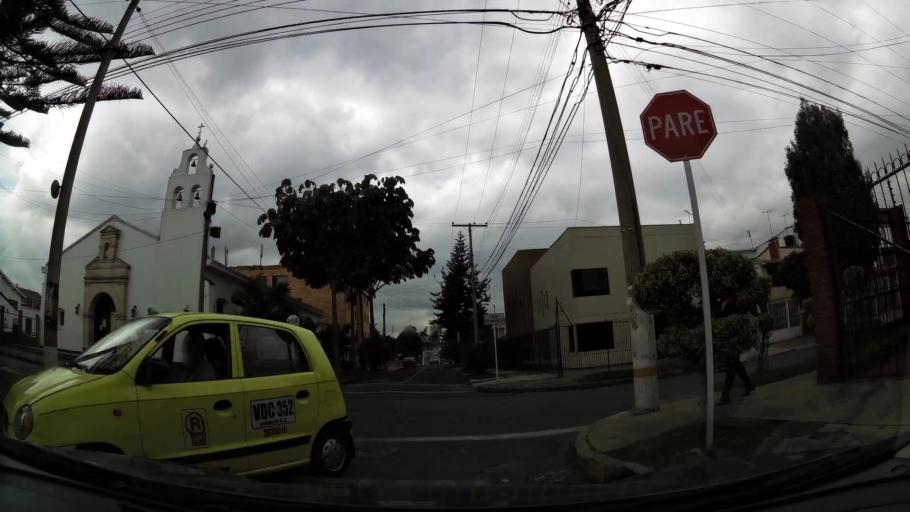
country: CO
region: Bogota D.C.
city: Barrio San Luis
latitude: 4.6841
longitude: -74.0705
